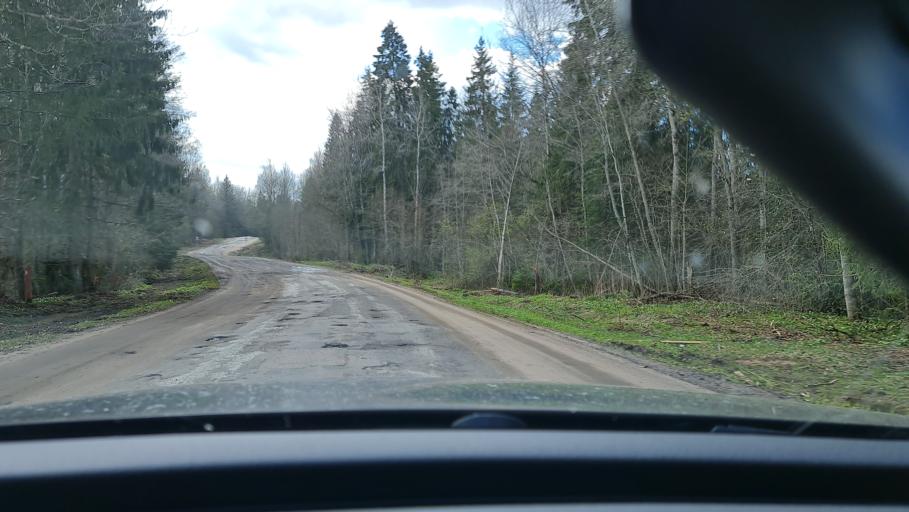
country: RU
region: Tverskaya
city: Toropets
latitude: 56.6232
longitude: 31.4299
